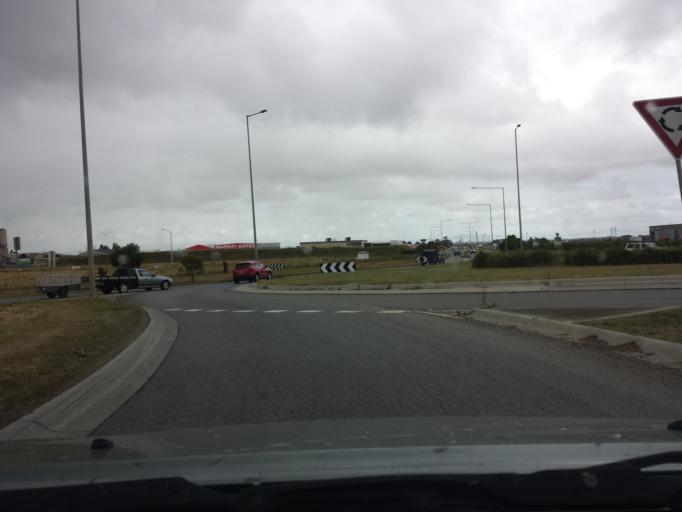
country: AU
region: Victoria
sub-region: Cardinia
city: Pakenham South
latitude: -38.0938
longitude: 145.4899
